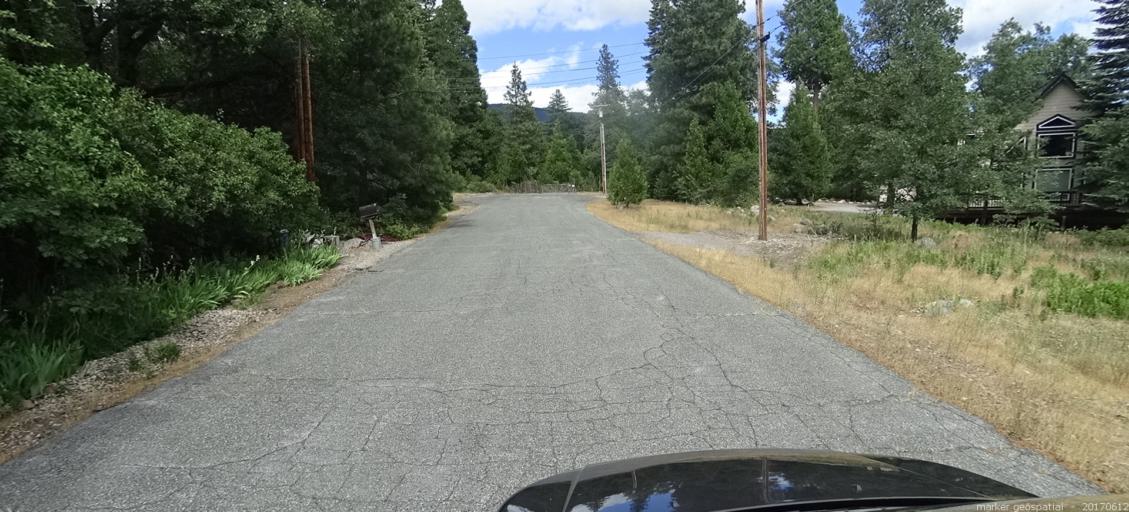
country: US
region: California
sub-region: Siskiyou County
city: Mount Shasta
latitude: 41.3260
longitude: -122.3100
